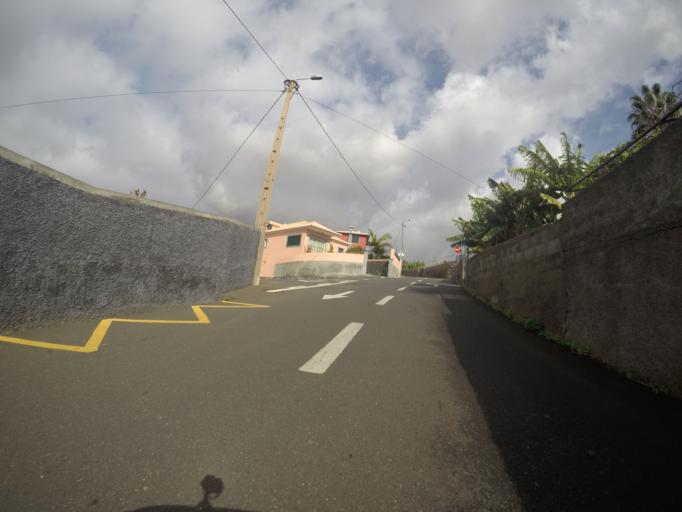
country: PT
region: Madeira
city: Camara de Lobos
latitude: 32.6483
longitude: -16.9518
